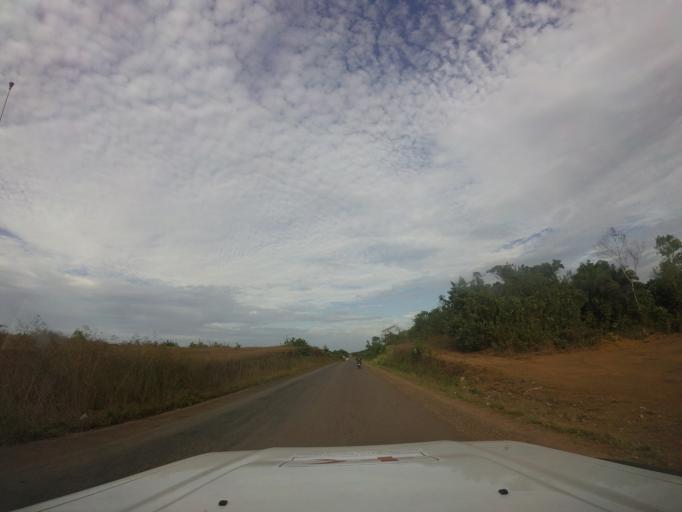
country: LR
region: Bomi
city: Tubmanburg
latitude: 6.7310
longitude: -11.0053
